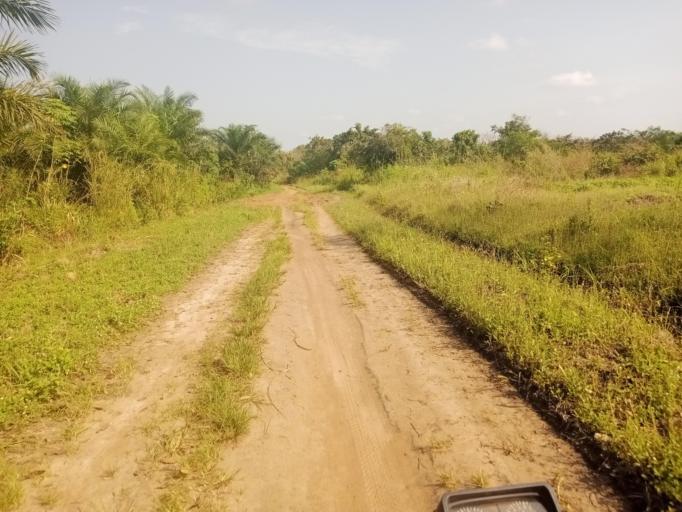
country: TG
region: Maritime
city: Tsevie
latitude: 6.6646
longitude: 0.9775
